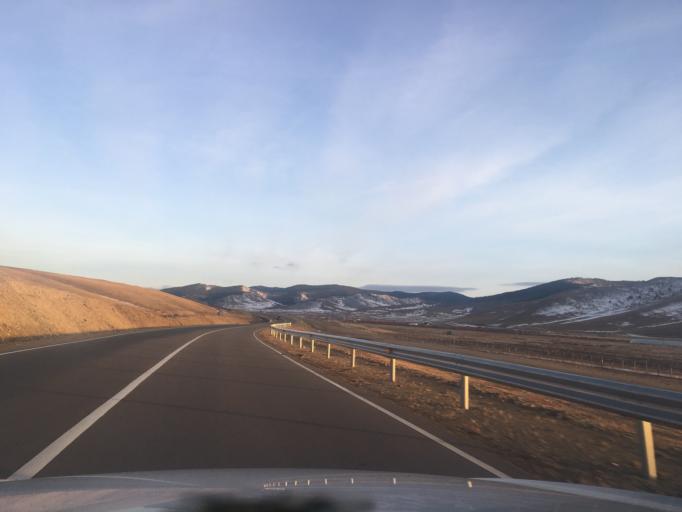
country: MN
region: Central Aimak
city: Mandal
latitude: 48.1105
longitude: 106.7112
